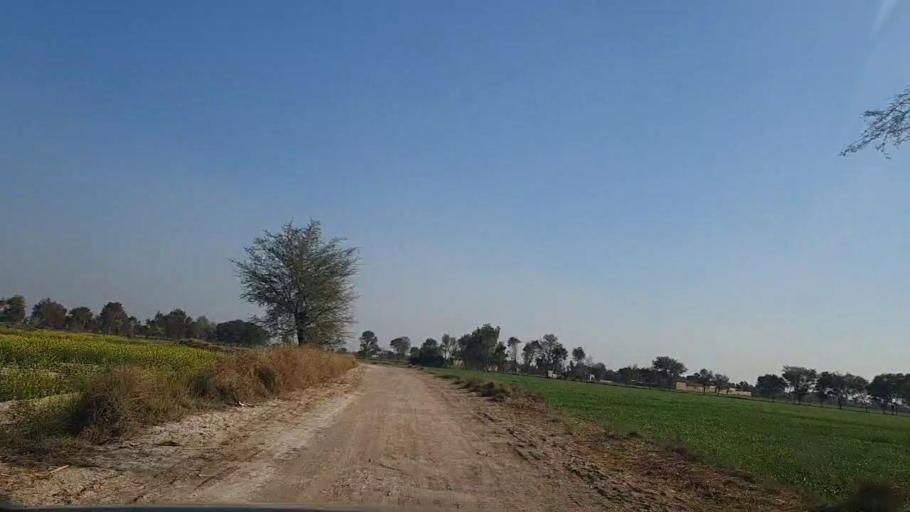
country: PK
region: Sindh
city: Daur
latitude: 26.3151
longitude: 68.1803
